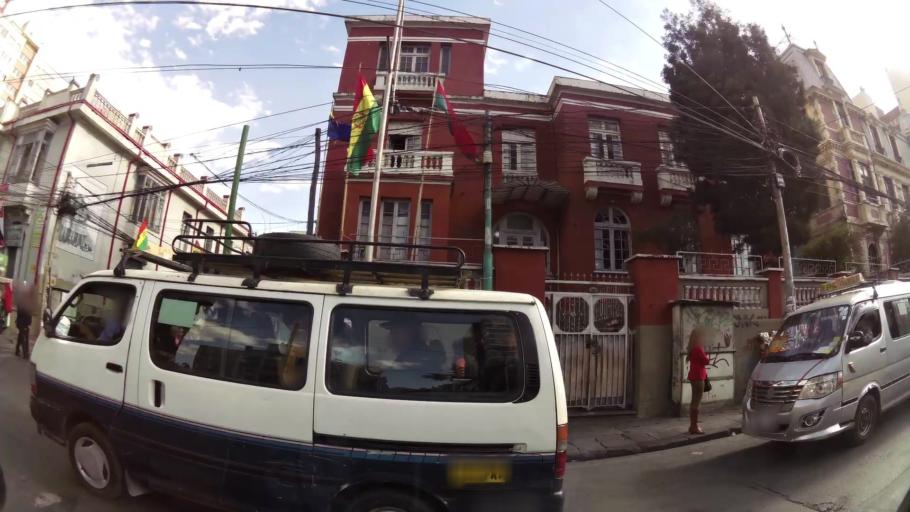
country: BO
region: La Paz
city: La Paz
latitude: -16.5065
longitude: -68.1288
